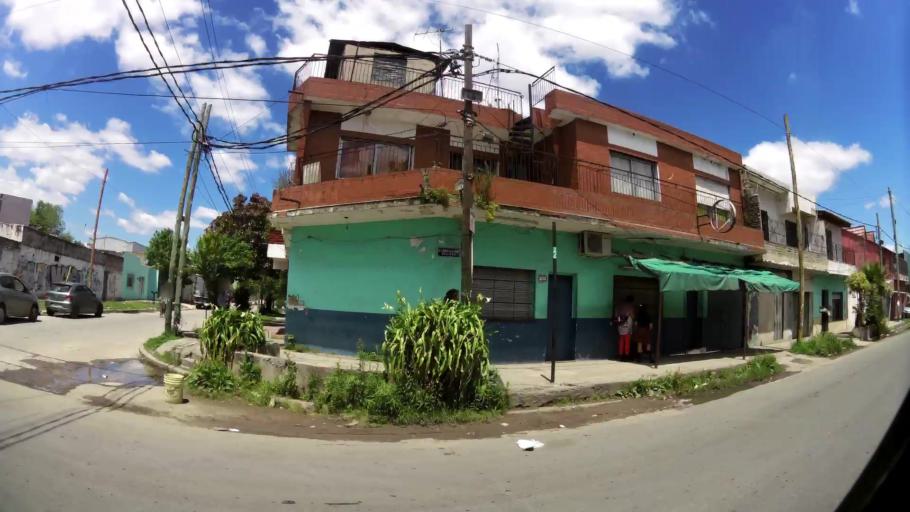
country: AR
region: Buenos Aires
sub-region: Partido de Lanus
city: Lanus
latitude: -34.7148
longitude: -58.4305
